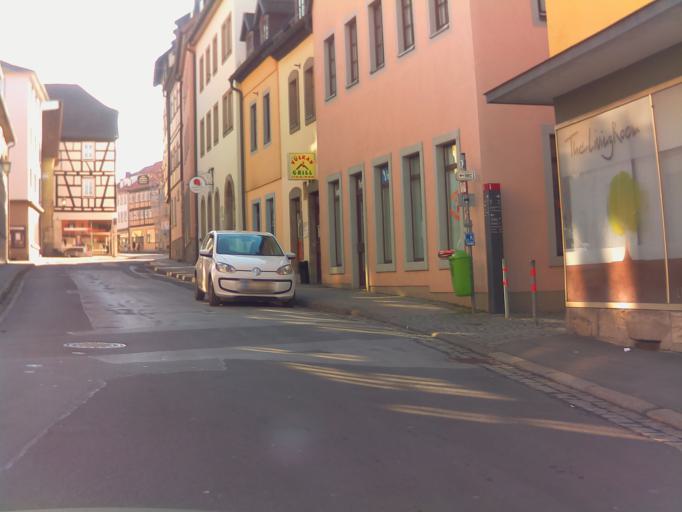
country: DE
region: Bavaria
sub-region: Regierungsbezirk Unterfranken
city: Munnerstadt
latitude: 50.2500
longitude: 10.1951
